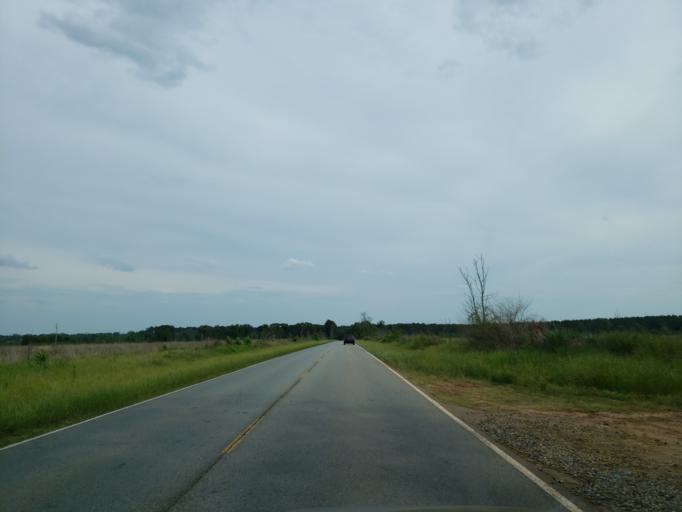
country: US
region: Georgia
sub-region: Macon County
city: Montezuma
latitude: 32.2160
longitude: -83.9314
